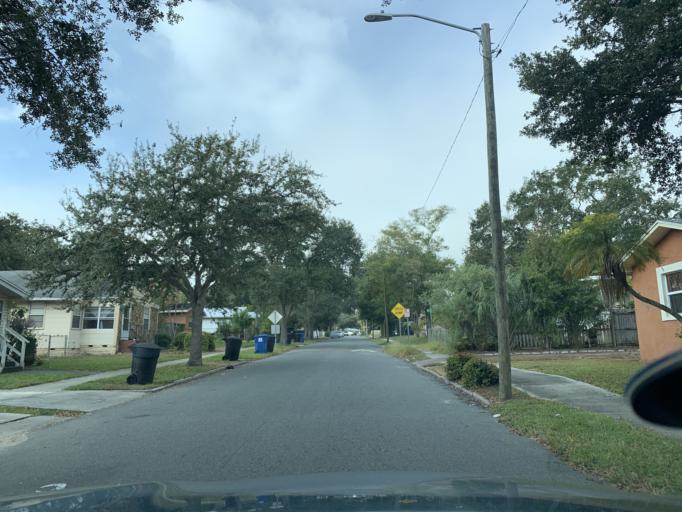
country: US
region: Florida
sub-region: Pinellas County
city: Saint Petersburg
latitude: 27.7556
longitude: -82.6437
